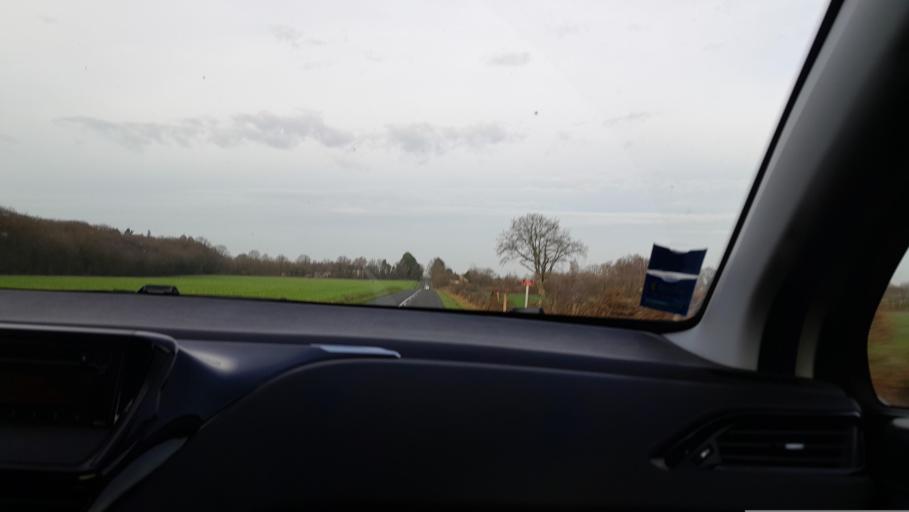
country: FR
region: Pays de la Loire
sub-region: Departement de la Mayenne
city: Ballots
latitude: 47.8856
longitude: -1.0294
